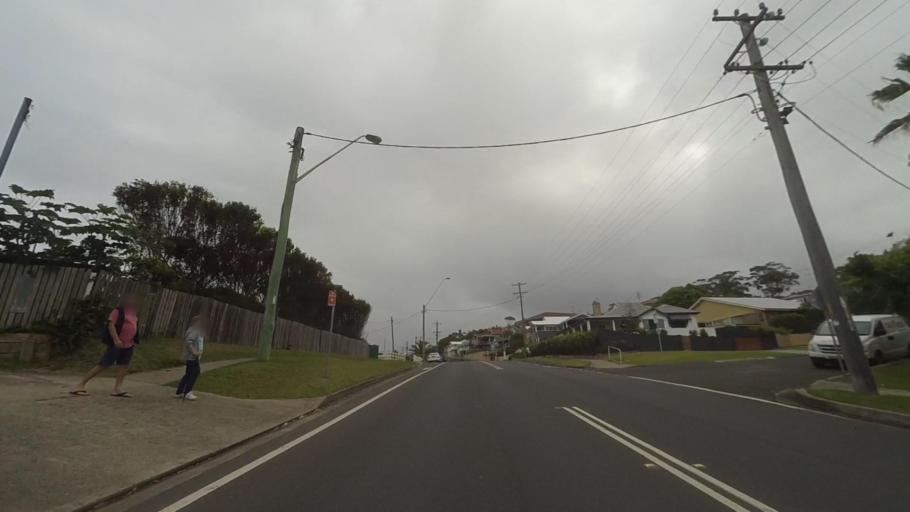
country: AU
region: New South Wales
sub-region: Wollongong
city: Bulli
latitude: -34.3081
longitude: 150.9334
